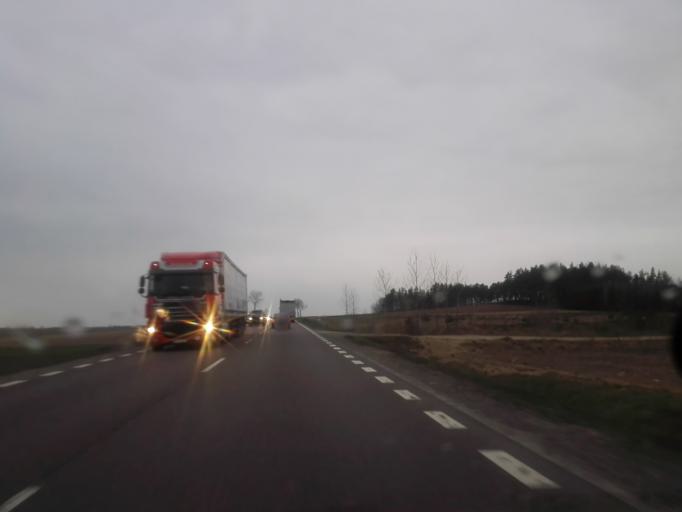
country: PL
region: Podlasie
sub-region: Powiat grajewski
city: Grajewo
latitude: 53.6163
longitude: 22.3886
